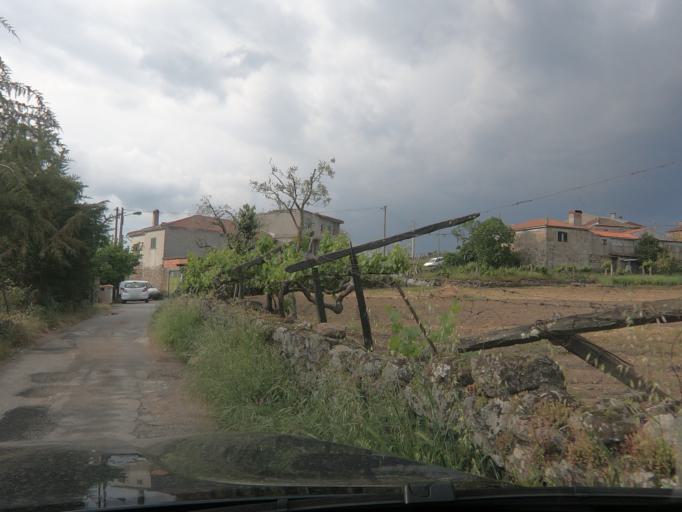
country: PT
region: Vila Real
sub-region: Vila Real
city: Vila Real
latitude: 41.3089
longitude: -7.7002
